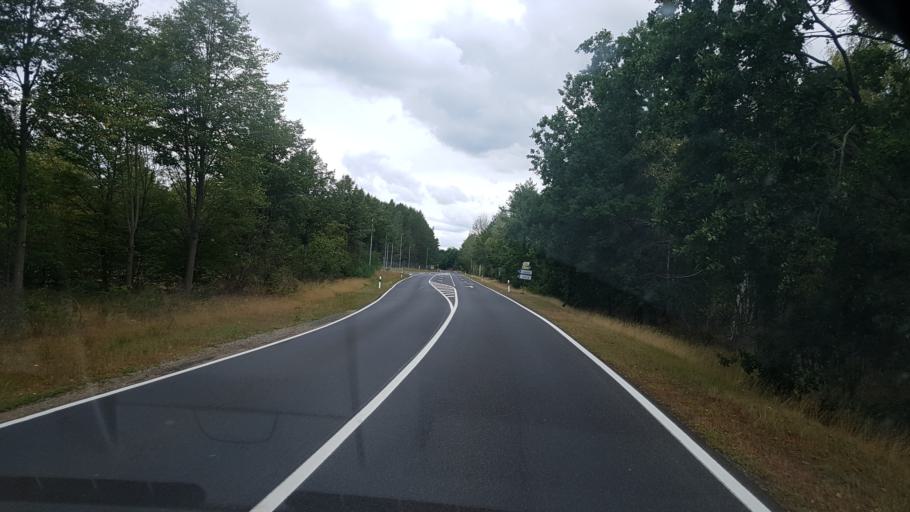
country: DE
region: Saxony
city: Boxberg
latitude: 51.3965
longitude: 14.5962
